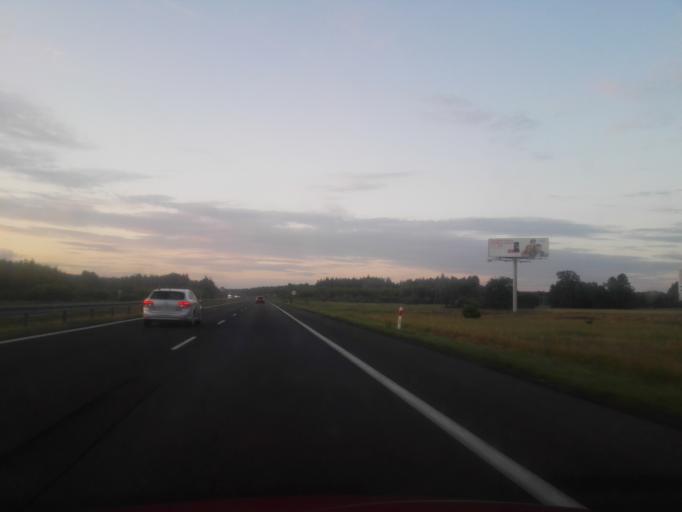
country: PL
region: Lodz Voivodeship
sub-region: Powiat radomszczanski
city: Radomsko
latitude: 51.0512
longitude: 19.3545
